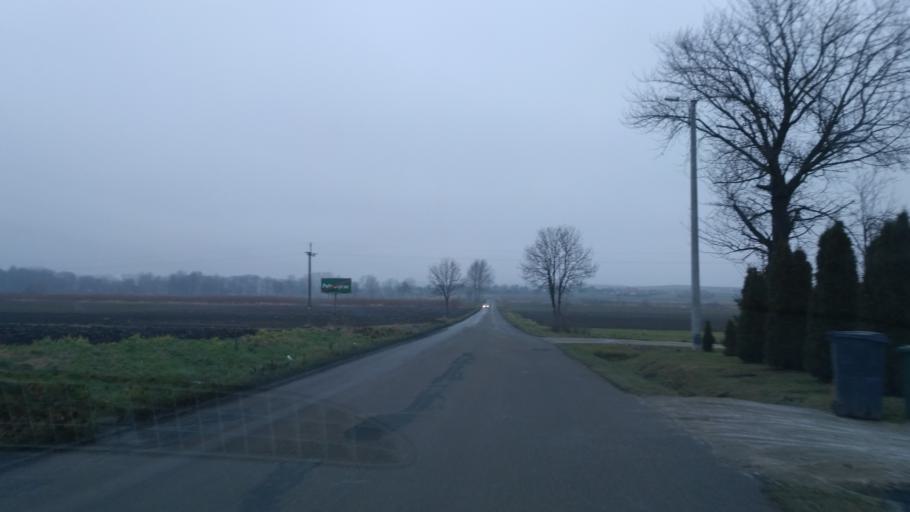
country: PL
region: Subcarpathian Voivodeship
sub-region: Powiat przeworski
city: Zarzecze
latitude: 49.9764
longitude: 22.5530
